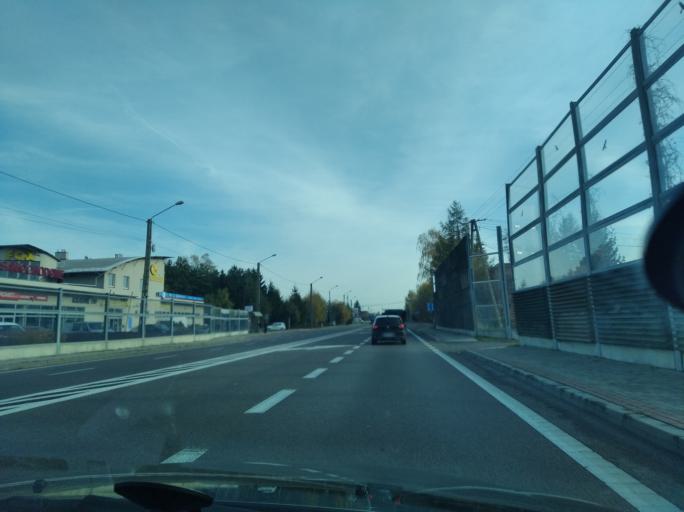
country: PL
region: Subcarpathian Voivodeship
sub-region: Powiat rzeszowski
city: Krasne
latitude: 50.0409
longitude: 22.0878
